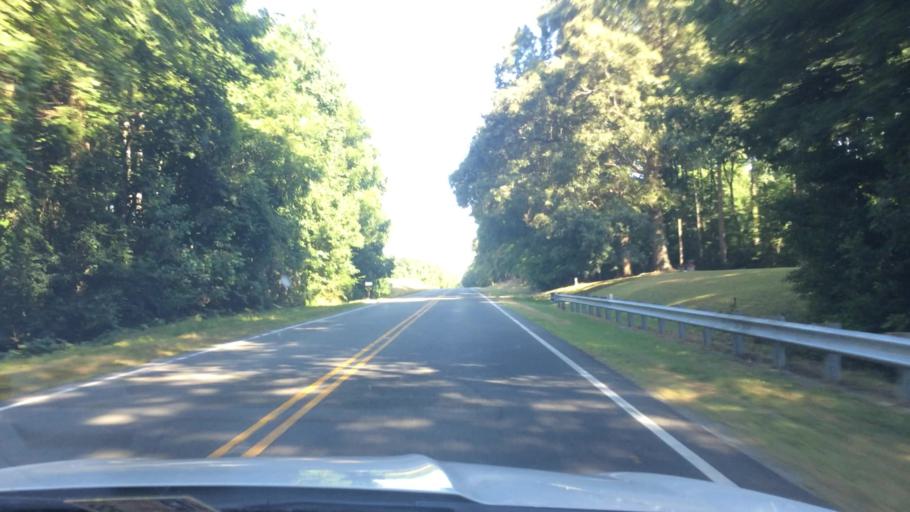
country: US
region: Virginia
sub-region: Lancaster County
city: Lancaster
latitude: 37.8012
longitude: -76.5311
